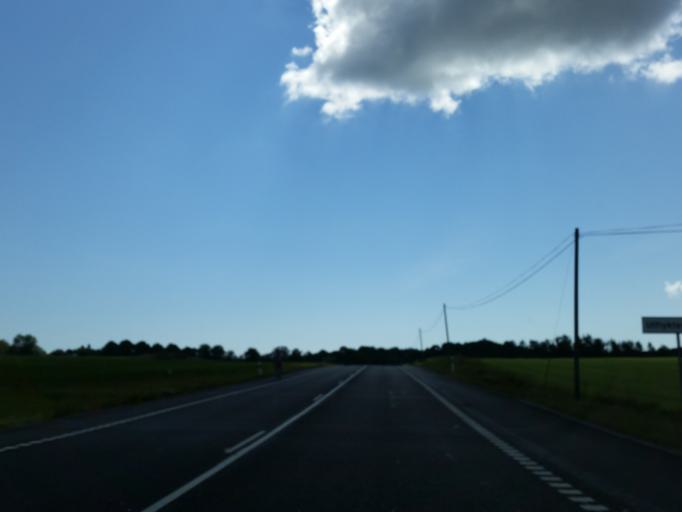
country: SE
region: Soedermanland
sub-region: Trosa Kommun
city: Vagnharad
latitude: 59.0122
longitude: 17.5953
